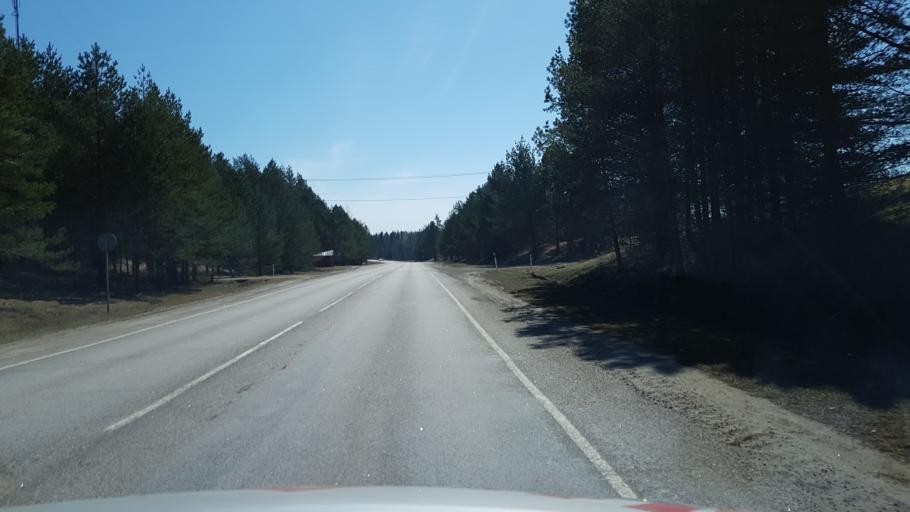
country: EE
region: Ida-Virumaa
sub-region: Johvi vald
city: Johvi
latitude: 59.1658
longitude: 27.3524
